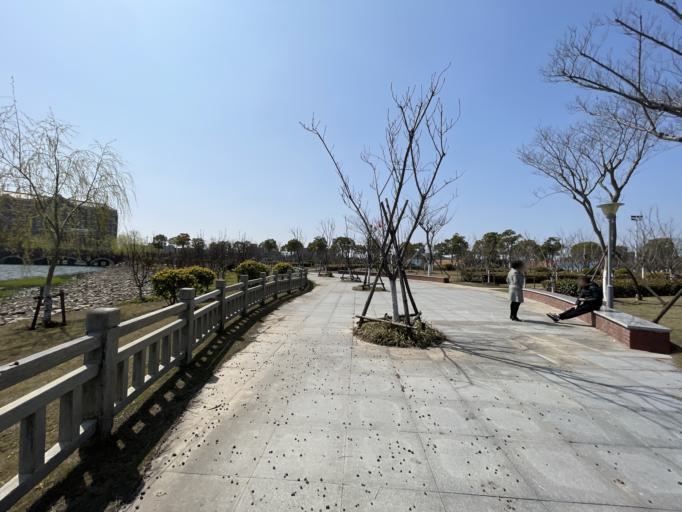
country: CN
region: Shanghai Shi
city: Shuyuan
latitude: 30.8939
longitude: 121.8856
